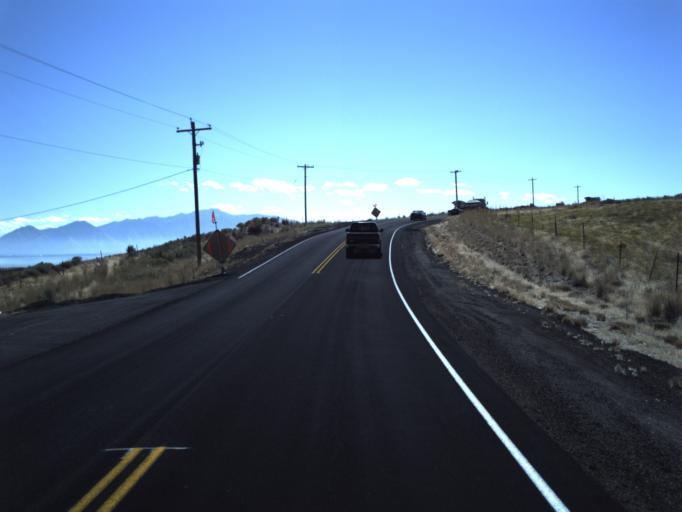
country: US
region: Utah
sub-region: Utah County
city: Saratoga Springs
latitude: 40.2758
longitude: -111.8676
